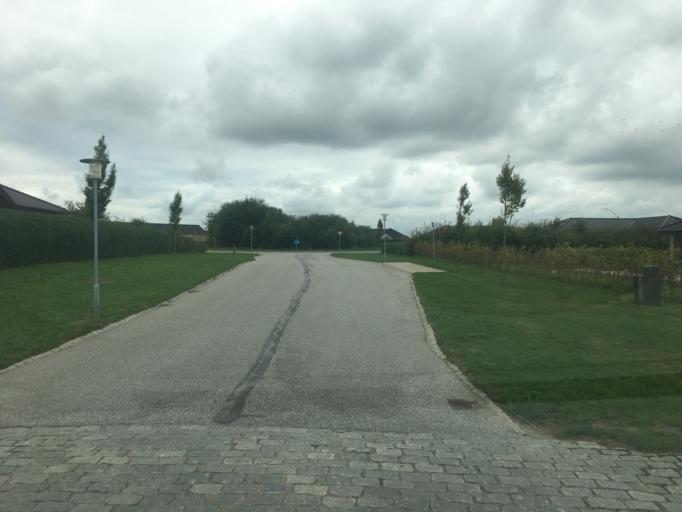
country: DK
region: South Denmark
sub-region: Tonder Kommune
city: Tonder
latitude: 54.9461
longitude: 8.8447
